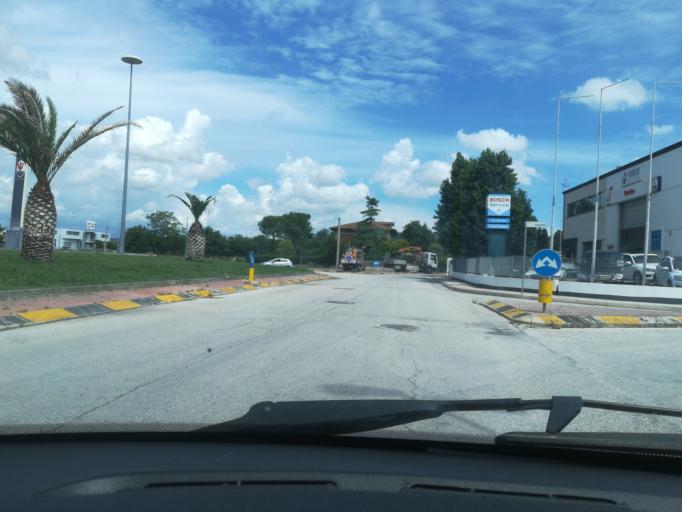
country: IT
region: The Marches
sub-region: Provincia di Macerata
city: Santa Maria Apparente
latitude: 43.2873
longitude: 13.6814
